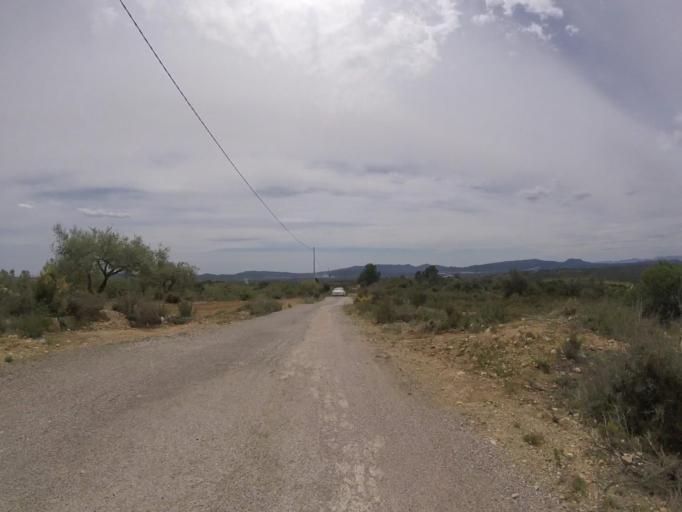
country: ES
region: Valencia
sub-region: Provincia de Castello
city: Sierra-Engarceran
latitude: 40.2226
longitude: -0.0204
